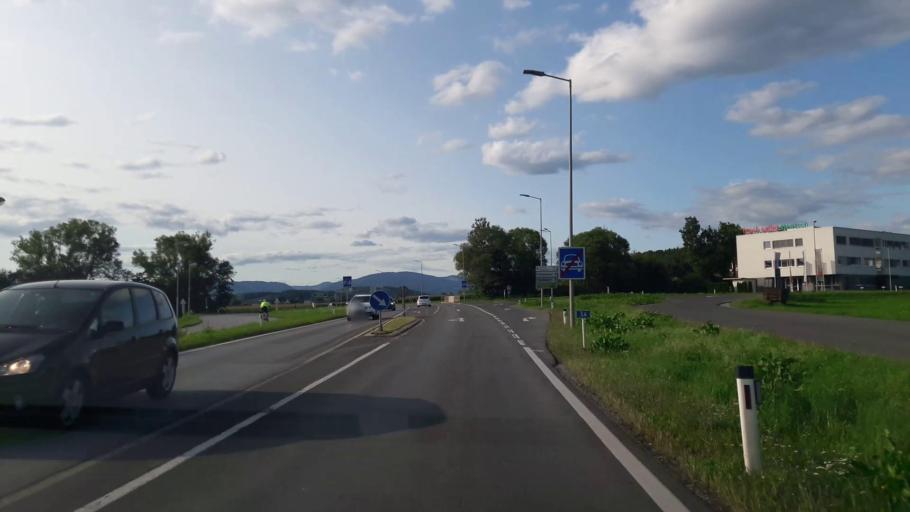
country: AT
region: Styria
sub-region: Politischer Bezirk Weiz
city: Sankt Ruprecht an der Raab
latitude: 47.1384
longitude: 15.6795
